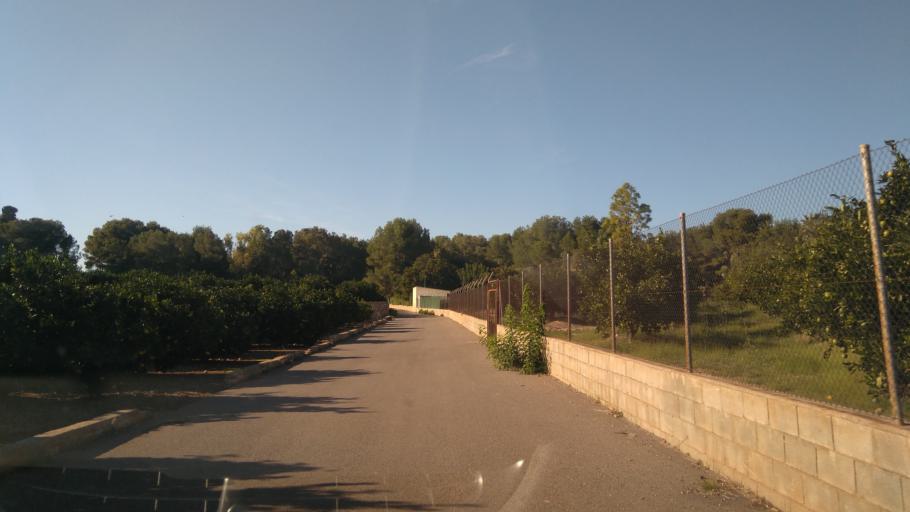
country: ES
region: Valencia
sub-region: Provincia de Valencia
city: Benimodo
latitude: 39.1769
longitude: -0.5570
